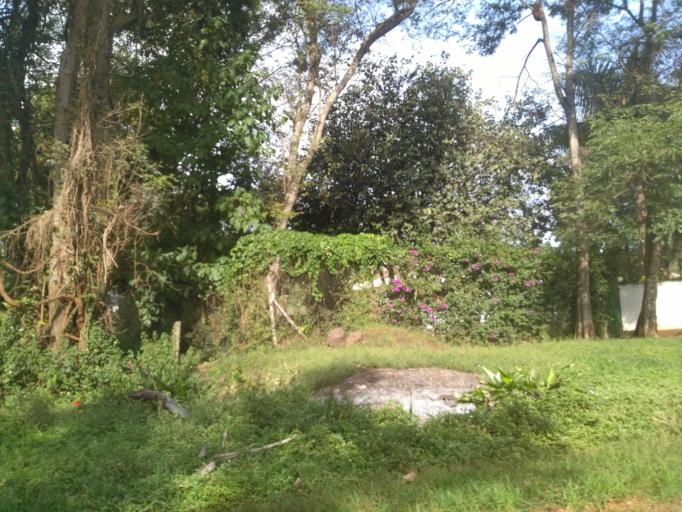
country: UG
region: Eastern Region
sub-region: Jinja District
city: Jinja
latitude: 0.4182
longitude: 33.1991
